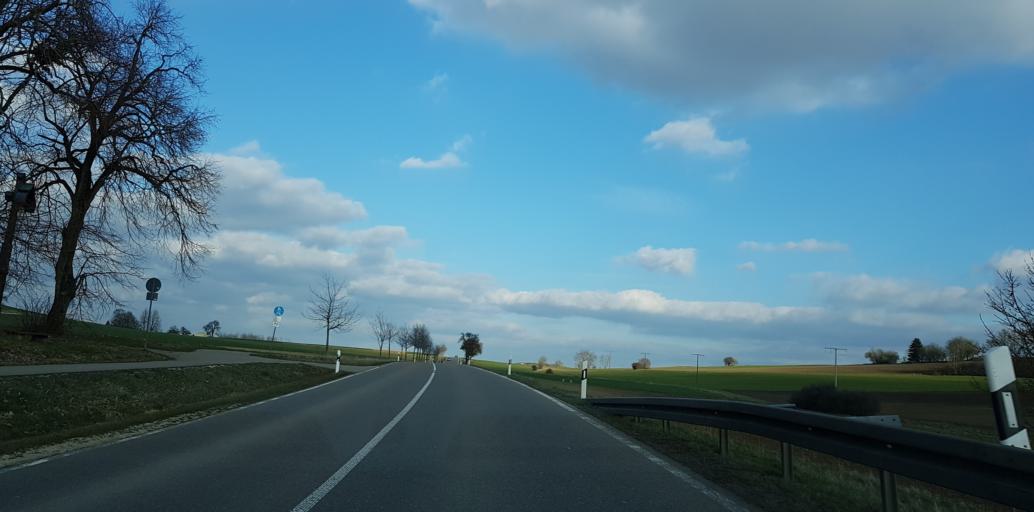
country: DE
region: Baden-Wuerttemberg
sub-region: Tuebingen Region
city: Altheim
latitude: 48.3228
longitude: 9.7497
